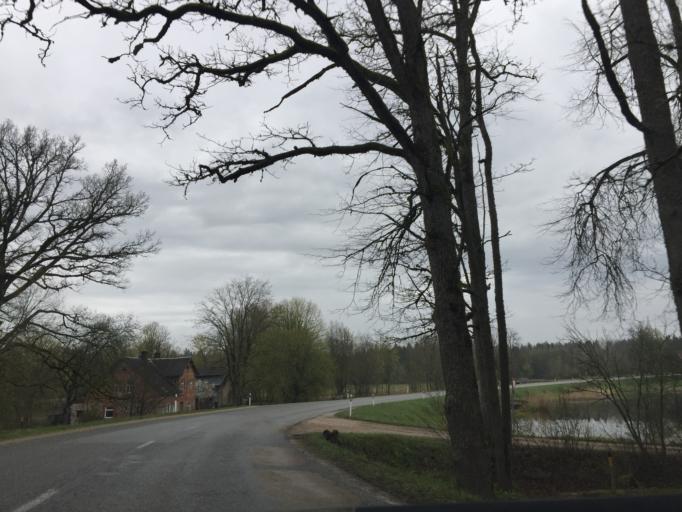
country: LV
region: Sigulda
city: Sigulda
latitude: 57.0283
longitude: 24.8160
